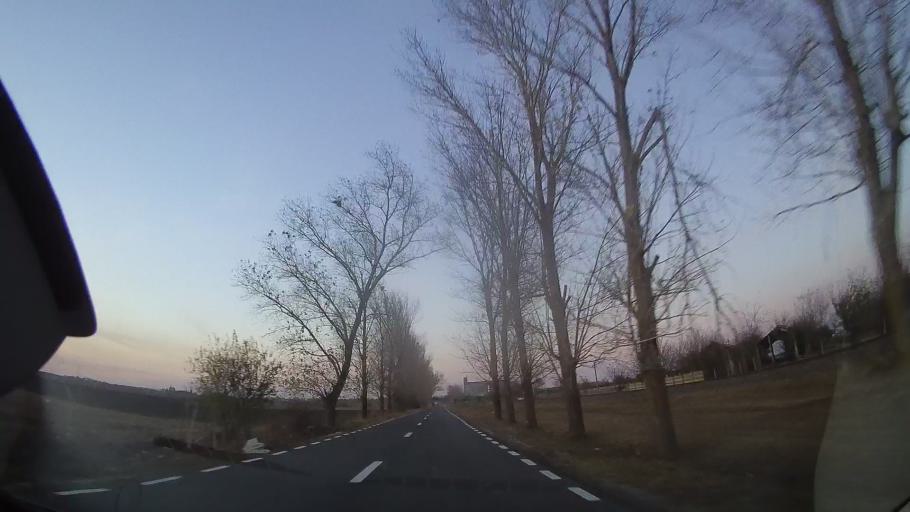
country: RO
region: Constanta
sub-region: Comuna Cobadin
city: Cobadin
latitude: 44.0455
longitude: 28.2530
